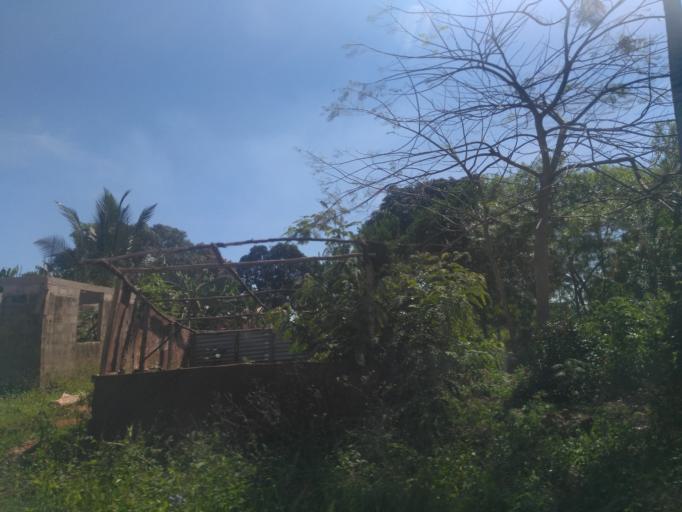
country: TZ
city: Kiwengwa
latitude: -5.9904
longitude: 39.3357
